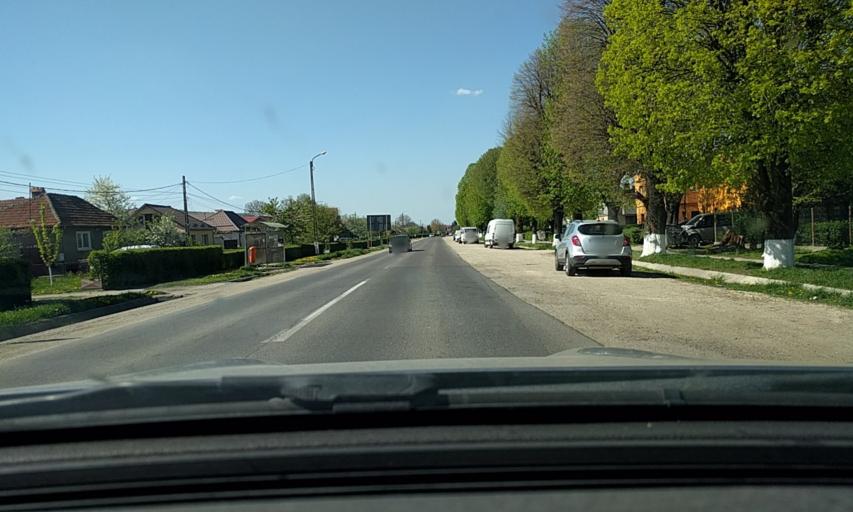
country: RO
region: Brasov
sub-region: Comuna Harman
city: Harman
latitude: 45.7018
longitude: 25.6899
